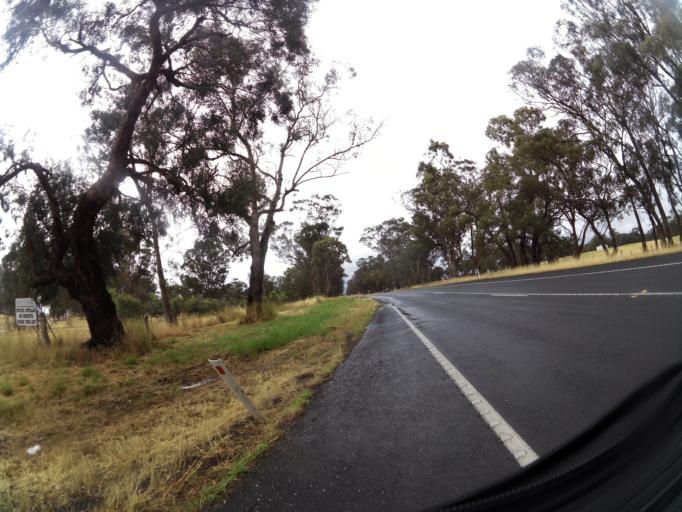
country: AU
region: Victoria
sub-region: Mount Alexander
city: Castlemaine
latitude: -37.0934
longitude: 144.1396
